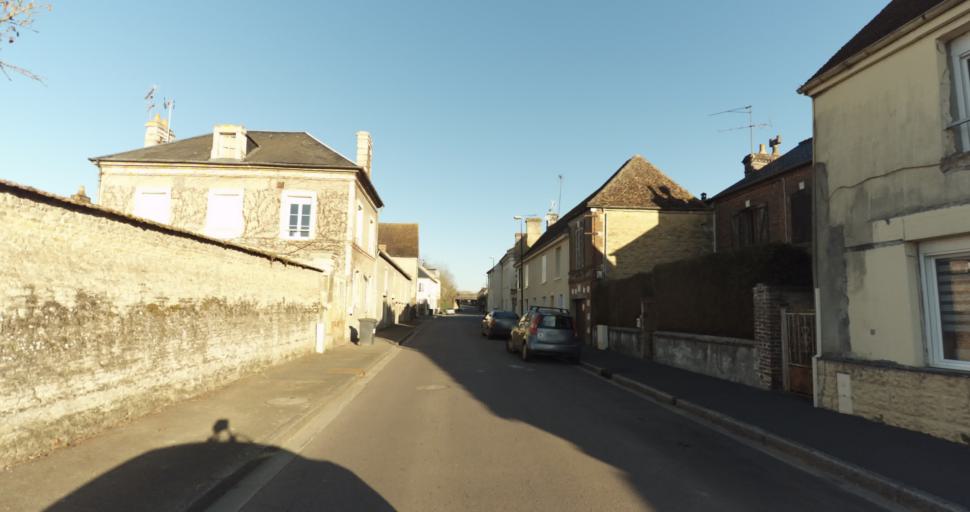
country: FR
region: Lower Normandy
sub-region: Departement du Calvados
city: Saint-Pierre-sur-Dives
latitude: 49.0232
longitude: -0.0378
